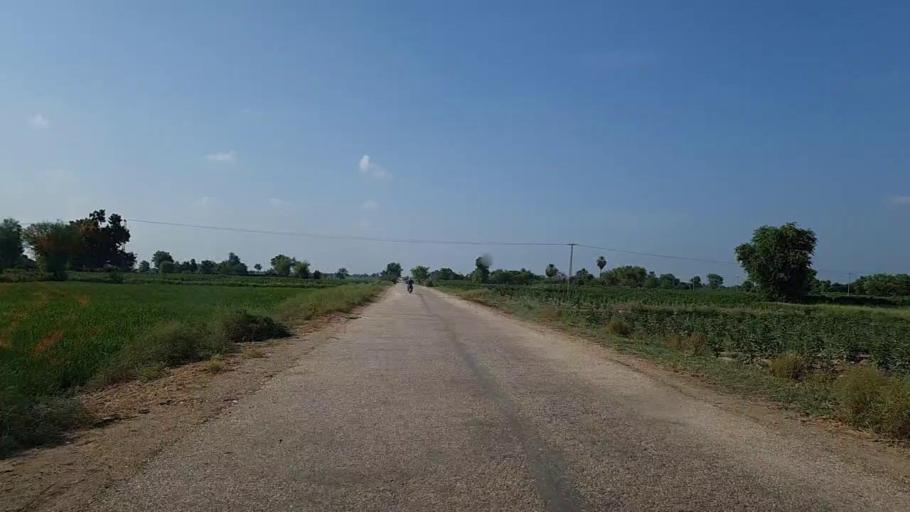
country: PK
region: Sindh
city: Kandiaro
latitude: 27.0568
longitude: 68.3171
